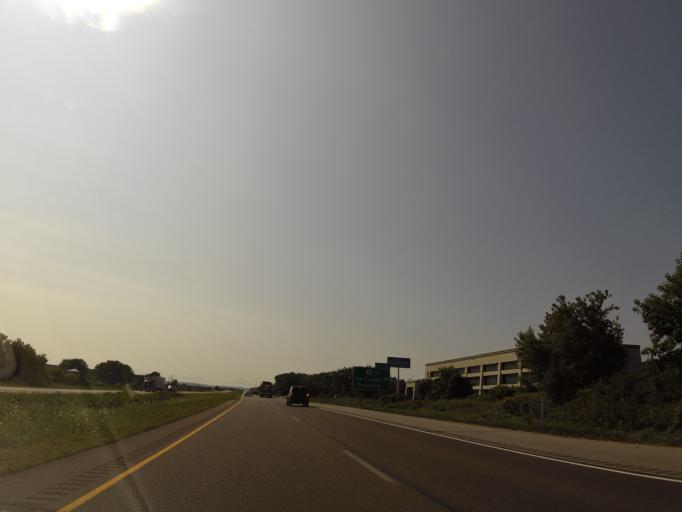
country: US
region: Wisconsin
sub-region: La Crosse County
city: Onalaska
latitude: 43.8763
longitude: -91.1732
